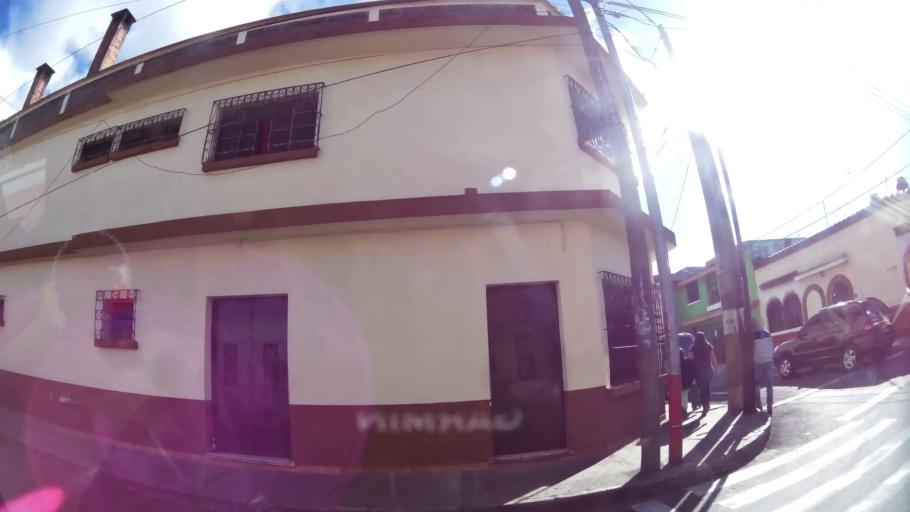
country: GT
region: Guatemala
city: Guatemala City
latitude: 14.6208
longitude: -90.5005
